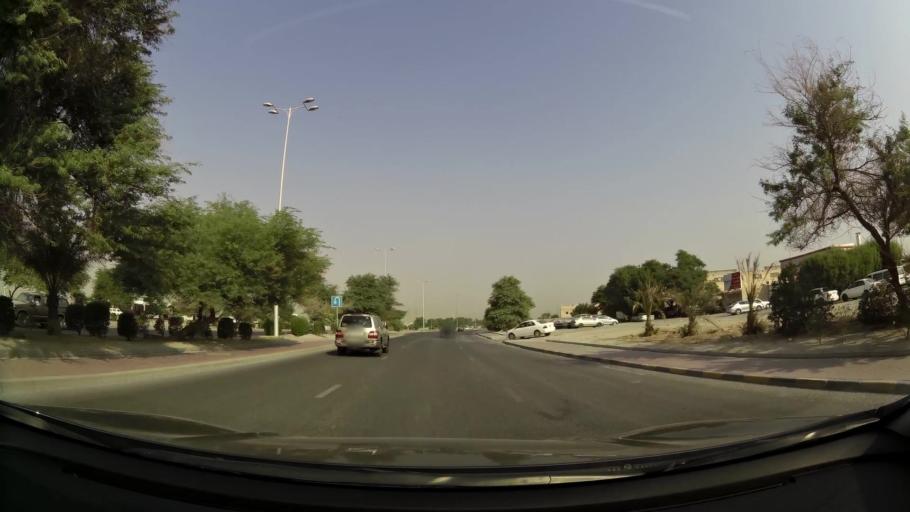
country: KW
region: Al Asimah
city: Ar Rabiyah
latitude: 29.2858
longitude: 47.8324
